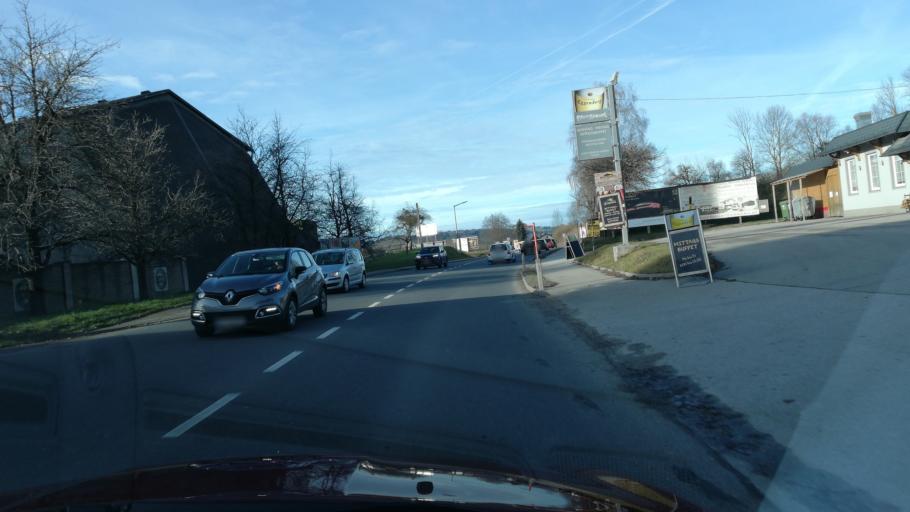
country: AT
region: Upper Austria
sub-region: Politischer Bezirk Kirchdorf an der Krems
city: Micheldorf in Oberoesterreich
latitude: 47.9096
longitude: 14.1172
